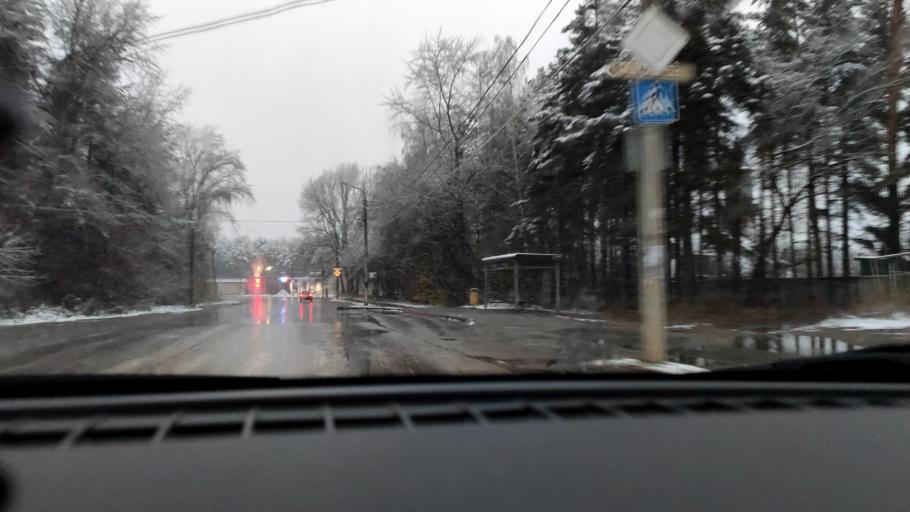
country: RU
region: Perm
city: Overyata
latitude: 58.0116
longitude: 55.9256
